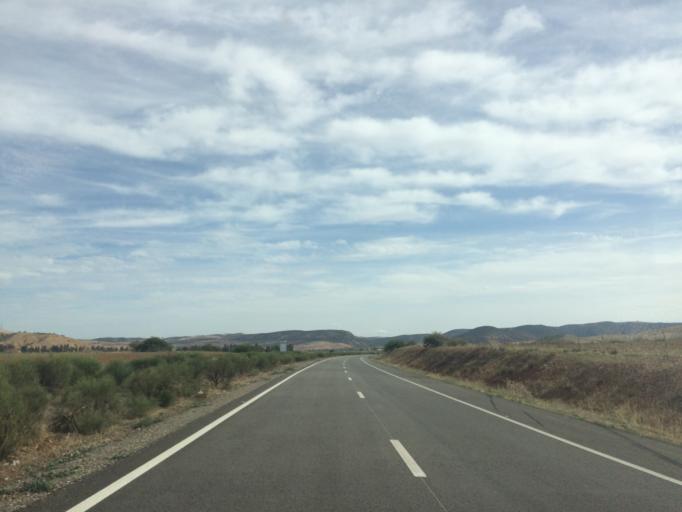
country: MA
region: Rabat-Sale-Zemmour-Zaer
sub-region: Khemisset
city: Khemisset
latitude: 33.7831
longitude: -5.9228
